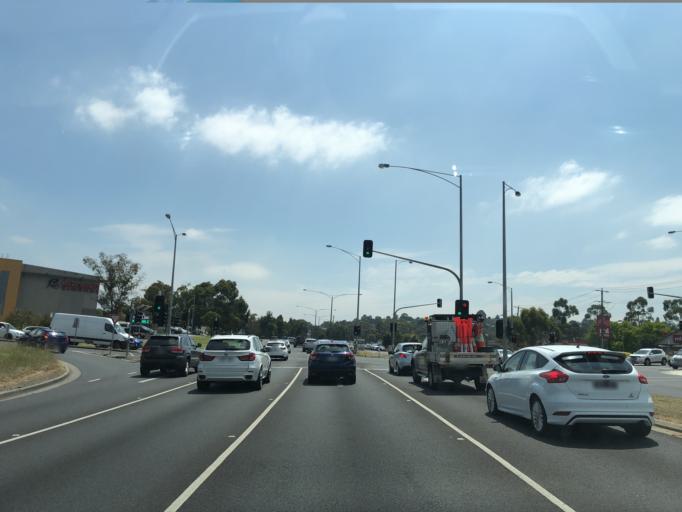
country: AU
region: Victoria
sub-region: Yarra Ranges
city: Chirnside Park
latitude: -37.7618
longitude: 145.3100
